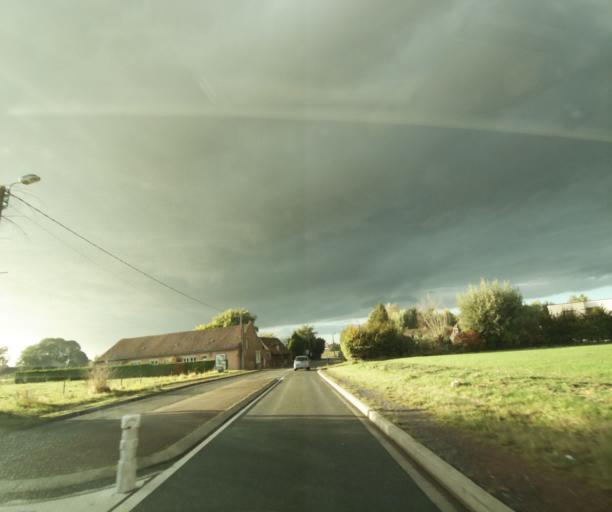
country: FR
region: Nord-Pas-de-Calais
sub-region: Departement du Nord
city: Roncq
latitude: 50.7411
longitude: 3.1142
